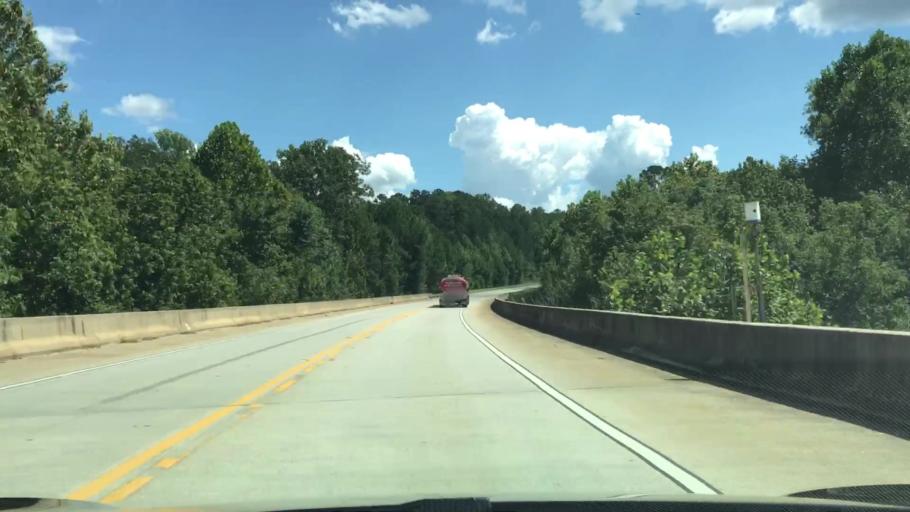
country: US
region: Georgia
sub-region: Oconee County
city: Watkinsville
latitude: 33.7208
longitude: -83.2957
